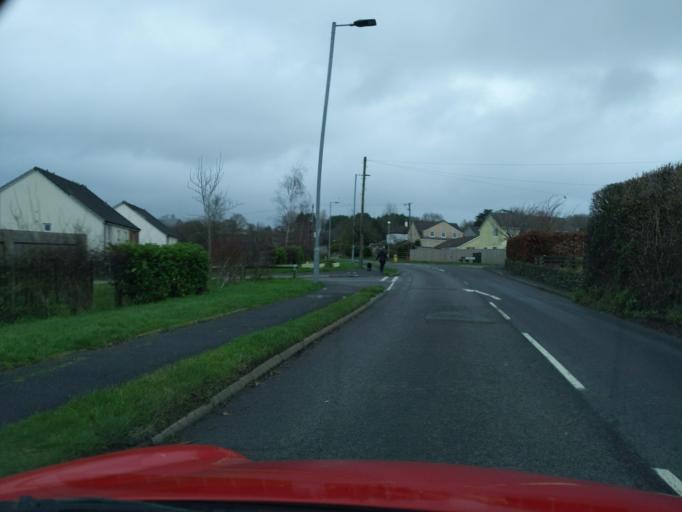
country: GB
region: England
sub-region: Cornwall
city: Werrington
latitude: 50.6882
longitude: -4.3217
